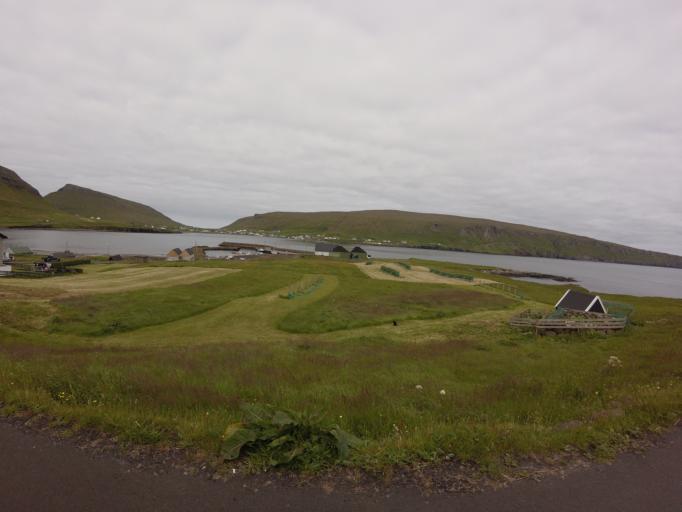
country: FO
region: Suduroy
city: Tvoroyri
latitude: 61.5926
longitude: -6.9288
